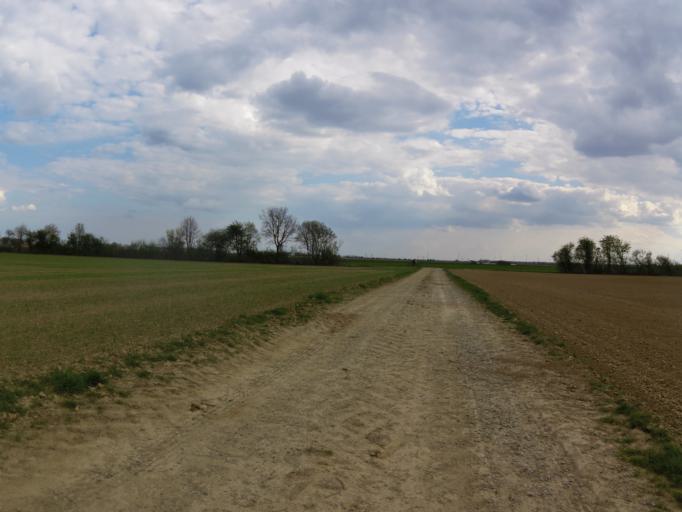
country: DE
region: Bavaria
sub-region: Regierungsbezirk Unterfranken
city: Oberpleichfeld
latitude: 49.8443
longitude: 10.0969
